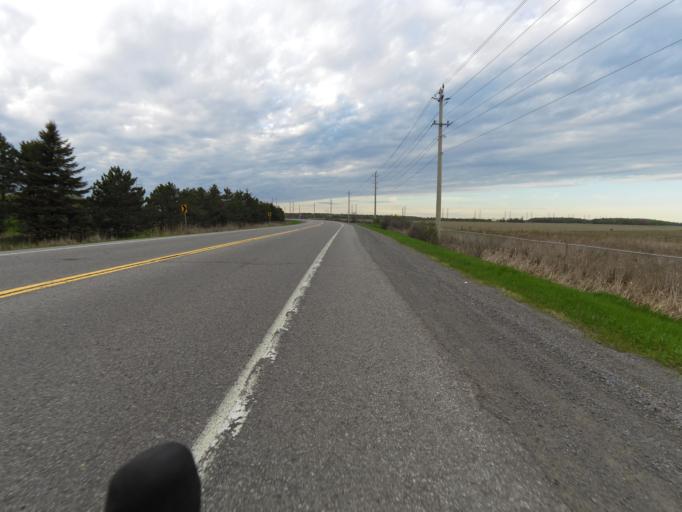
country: CA
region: Ontario
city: Bells Corners
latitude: 45.2992
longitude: -75.7914
